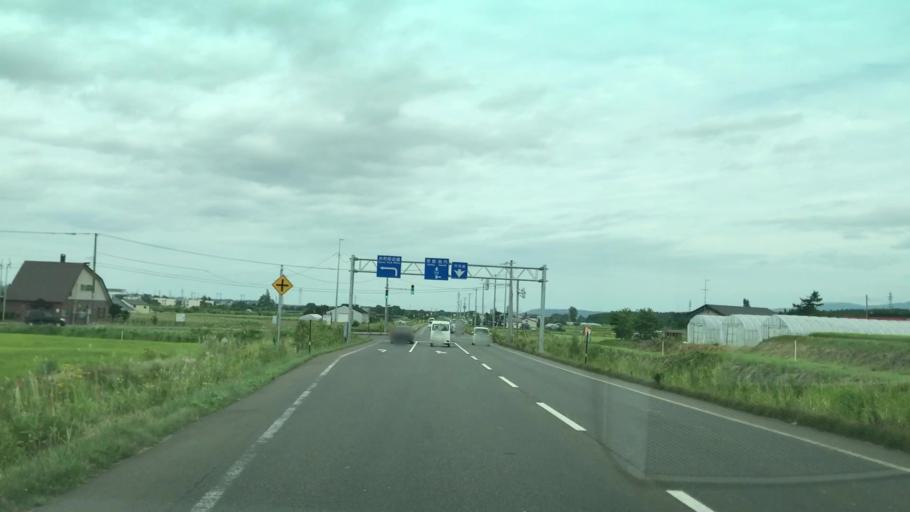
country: JP
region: Hokkaido
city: Iwanai
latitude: 42.9802
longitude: 140.6236
